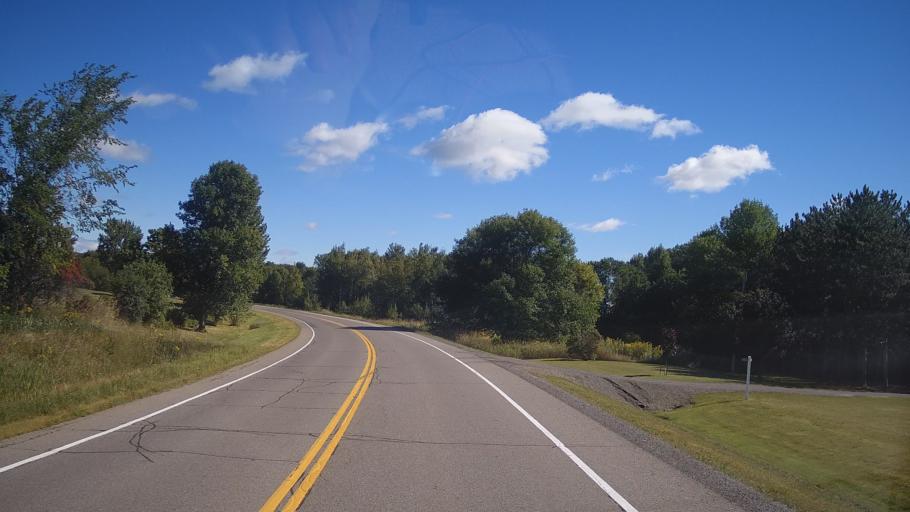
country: US
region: New York
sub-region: St. Lawrence County
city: Norfolk
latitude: 44.9509
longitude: -75.2818
